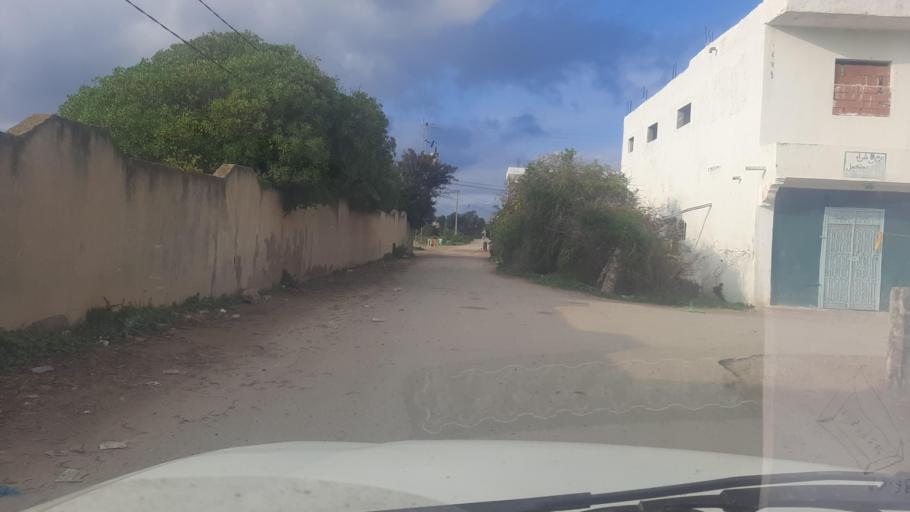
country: TN
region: Nabul
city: Manzil Bu Zalafah
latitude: 36.7162
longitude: 10.4967
